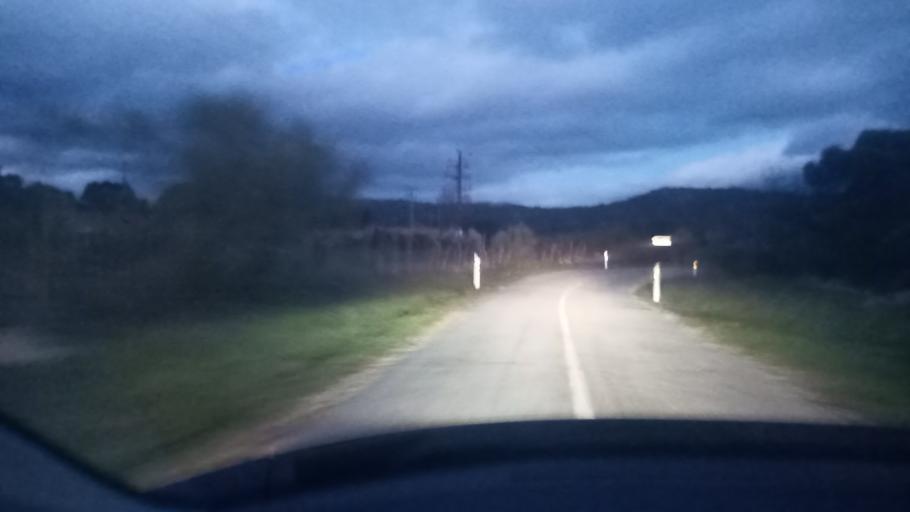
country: ES
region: Madrid
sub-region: Provincia de Madrid
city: Colmenar del Arroyo
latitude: 40.4467
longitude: -4.2305
